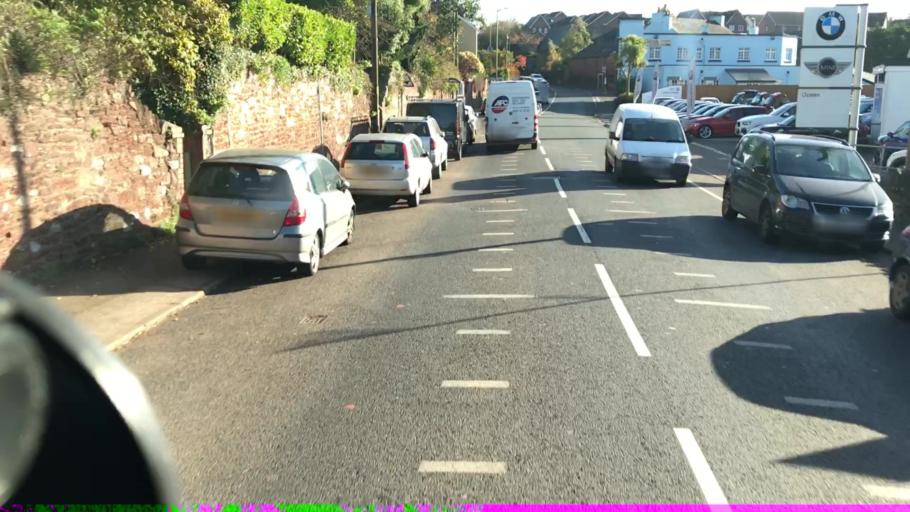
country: GB
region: England
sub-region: Devon
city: Marldon
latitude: 50.4291
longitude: -3.5984
